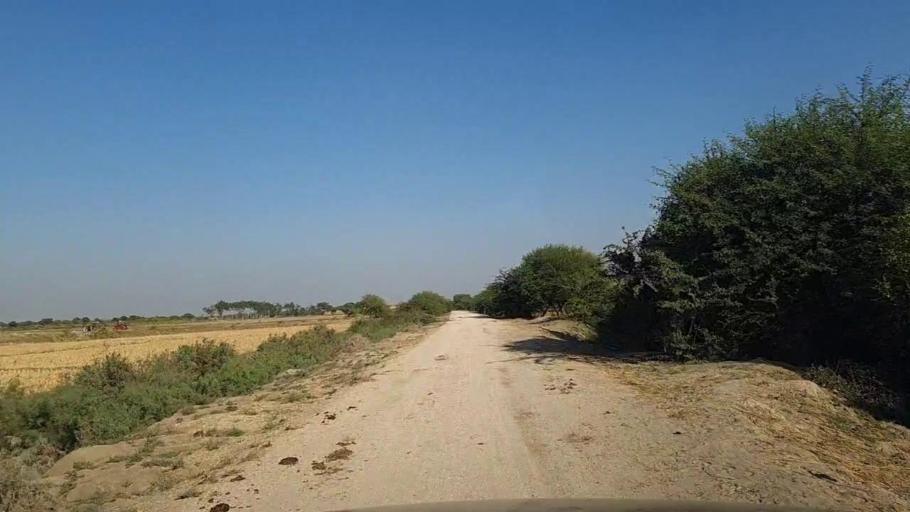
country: PK
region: Sindh
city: Mirpur Batoro
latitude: 24.7250
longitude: 68.3329
